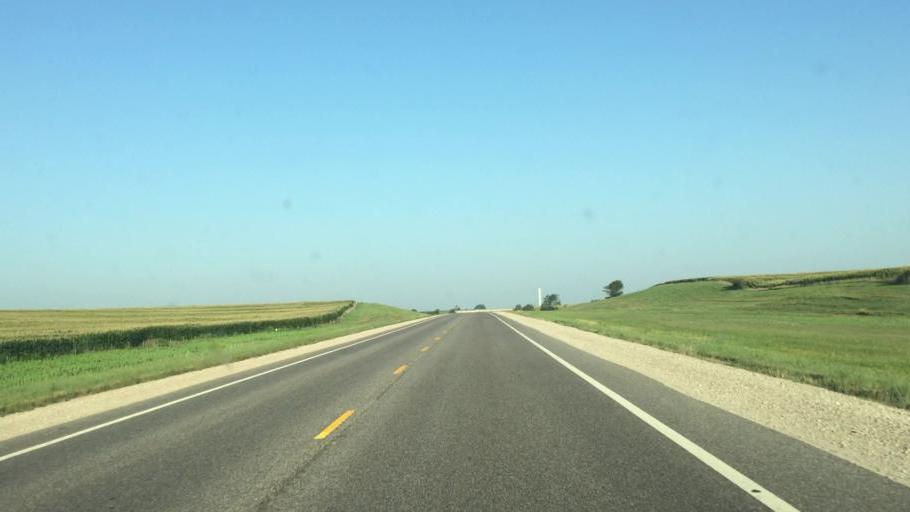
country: US
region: Kansas
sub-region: Doniphan County
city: Highland
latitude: 39.8422
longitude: -95.3253
